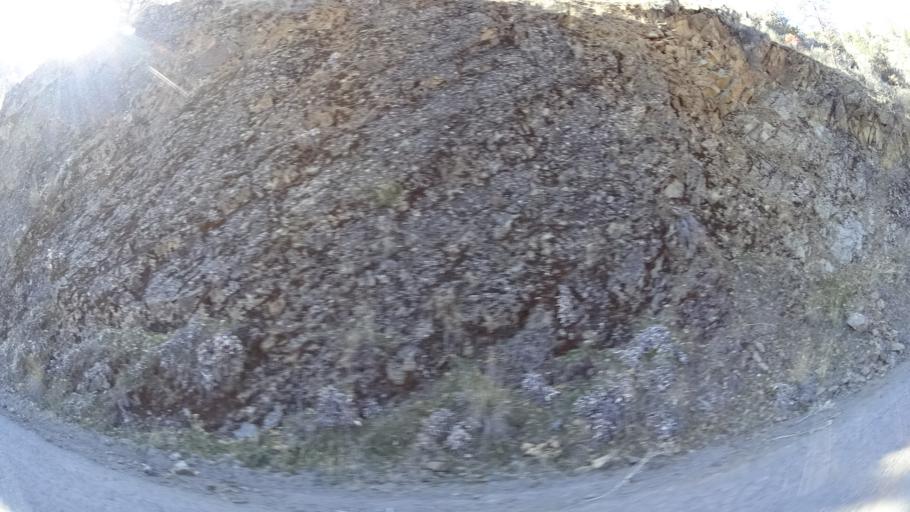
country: US
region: California
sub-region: Siskiyou County
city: Yreka
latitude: 41.7921
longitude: -122.6110
